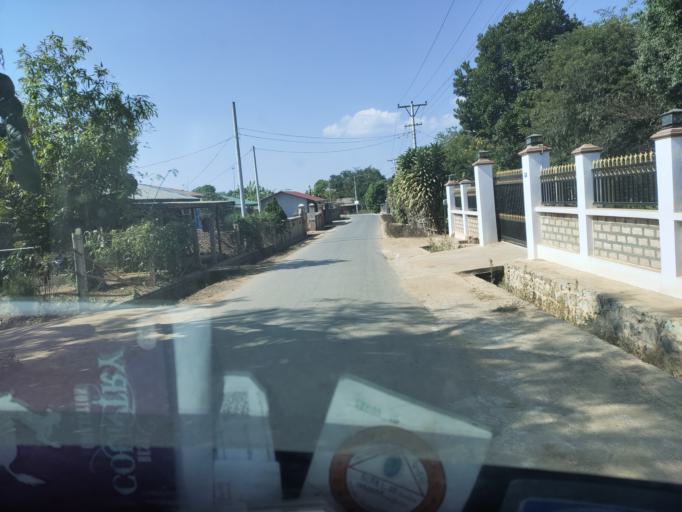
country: MM
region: Mandalay
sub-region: Pyin Oo Lwin District
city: Pyin Oo Lwin
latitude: 21.9537
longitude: 96.3912
